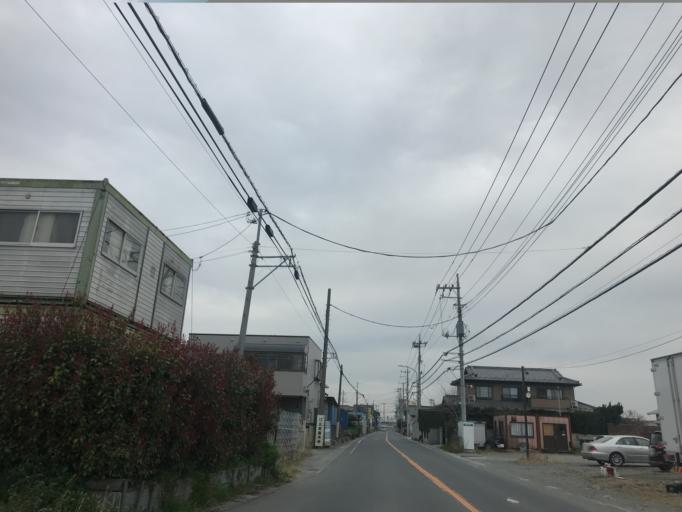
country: JP
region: Saitama
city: Yashio-shi
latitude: 35.8372
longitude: 139.8412
